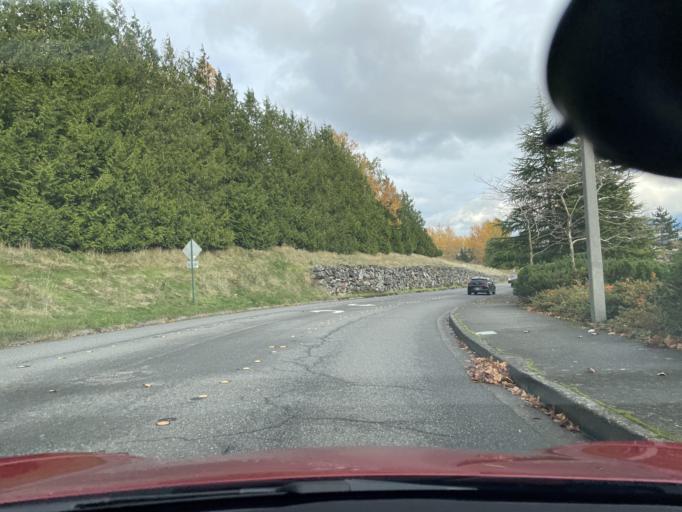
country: US
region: Washington
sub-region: Whatcom County
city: Bellingham
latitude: 48.7877
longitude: -122.4955
